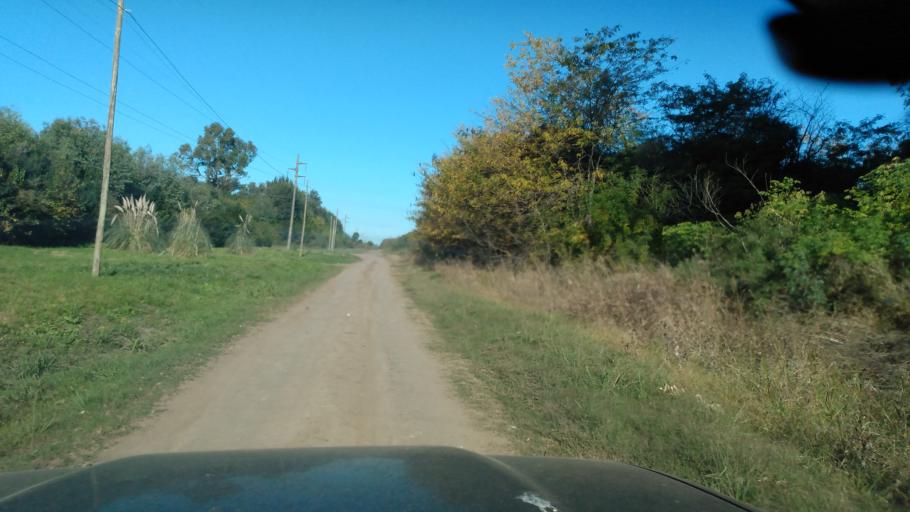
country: AR
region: Buenos Aires
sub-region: Partido de Lujan
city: Lujan
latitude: -34.5533
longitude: -59.1502
